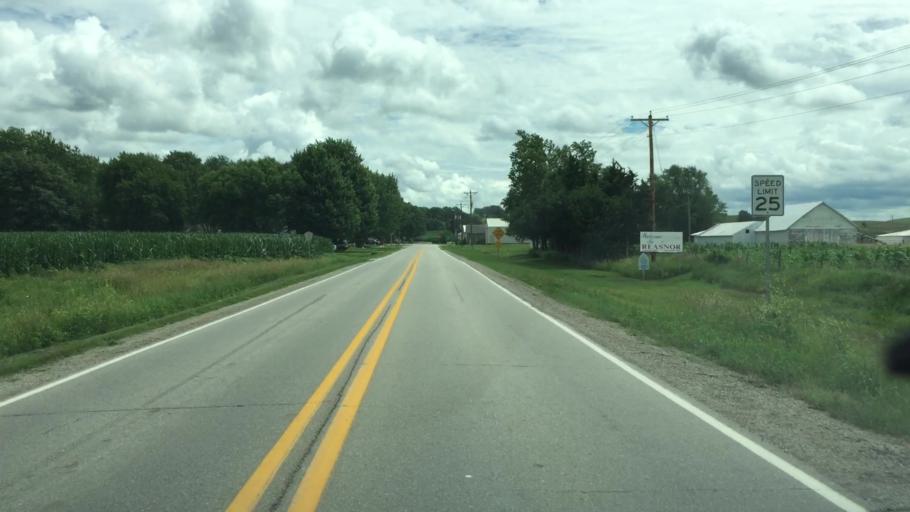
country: US
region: Iowa
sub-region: Jasper County
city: Monroe
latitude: 41.5770
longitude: -93.0271
